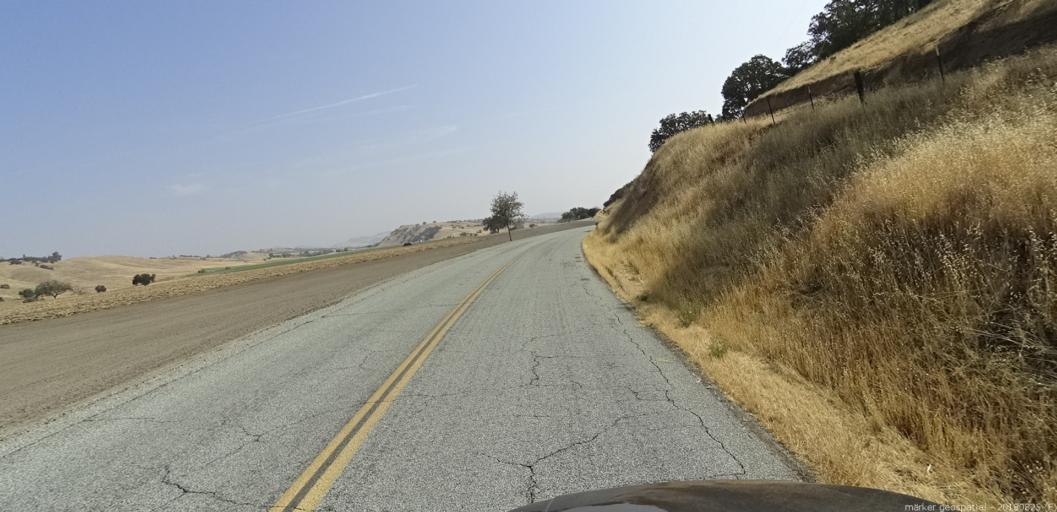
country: US
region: California
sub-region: San Luis Obispo County
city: San Miguel
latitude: 35.8155
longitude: -120.6639
